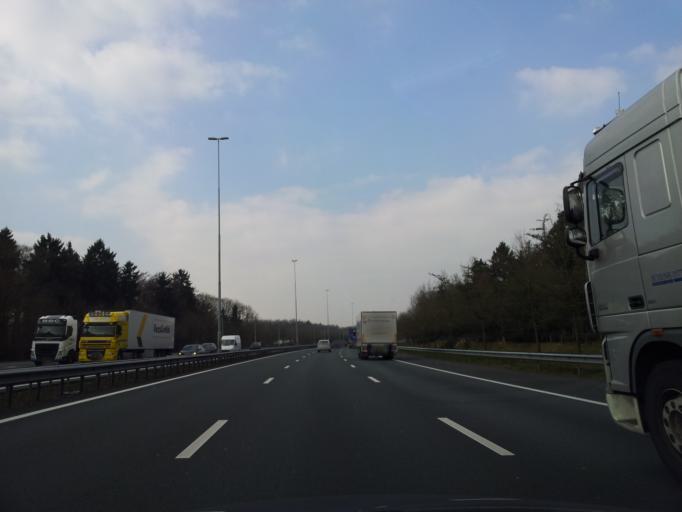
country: NL
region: North Brabant
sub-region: Gemeente Boxtel
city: Boxtel
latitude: 51.6102
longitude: 5.3223
